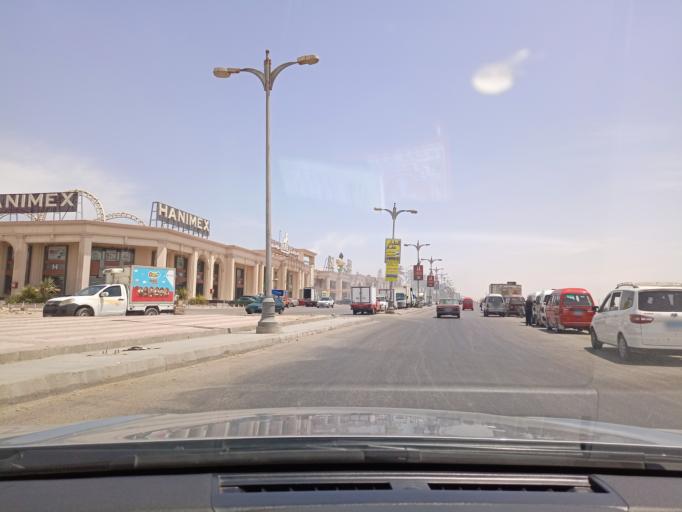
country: EG
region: Muhafazat al Qalyubiyah
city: Al Khankah
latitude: 30.1709
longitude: 31.4764
